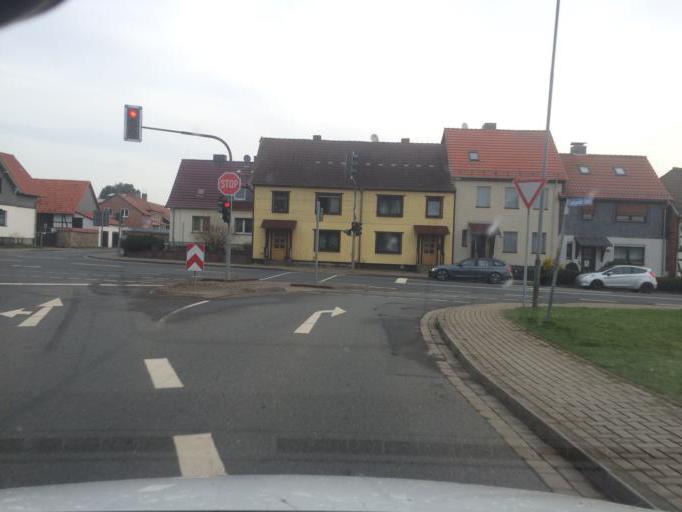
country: DE
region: Lower Saxony
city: Bad Sachsa
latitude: 51.5511
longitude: 10.5442
